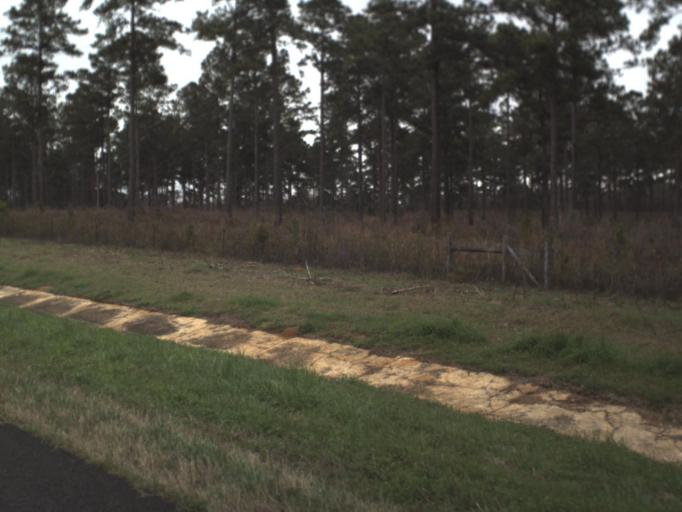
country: US
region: Florida
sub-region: Jefferson County
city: Monticello
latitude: 30.3970
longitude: -83.8750
